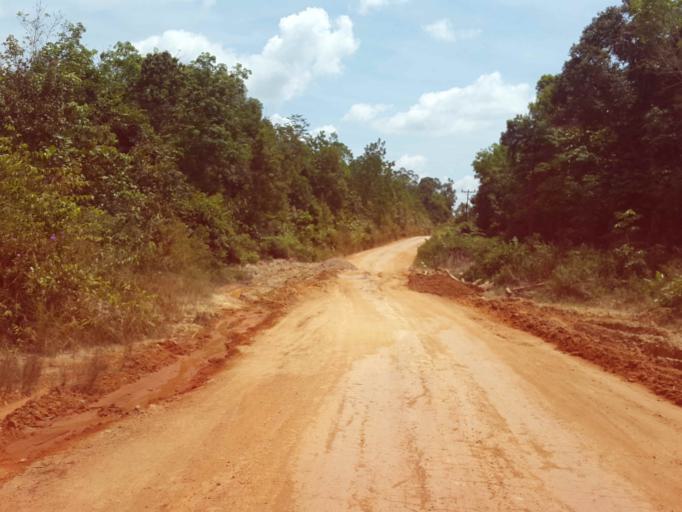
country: MY
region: Sarawak
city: Simanggang
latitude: 0.6025
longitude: 111.3675
